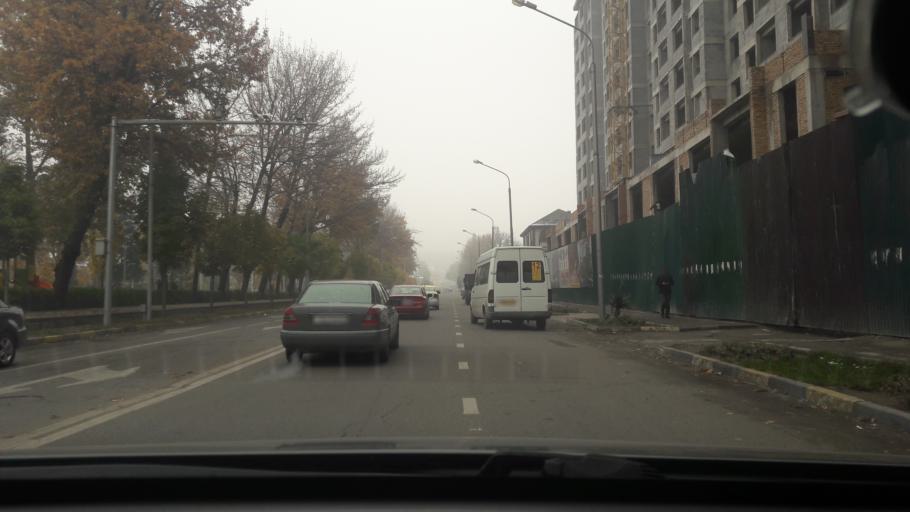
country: TJ
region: Dushanbe
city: Dushanbe
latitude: 38.5787
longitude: 68.7940
